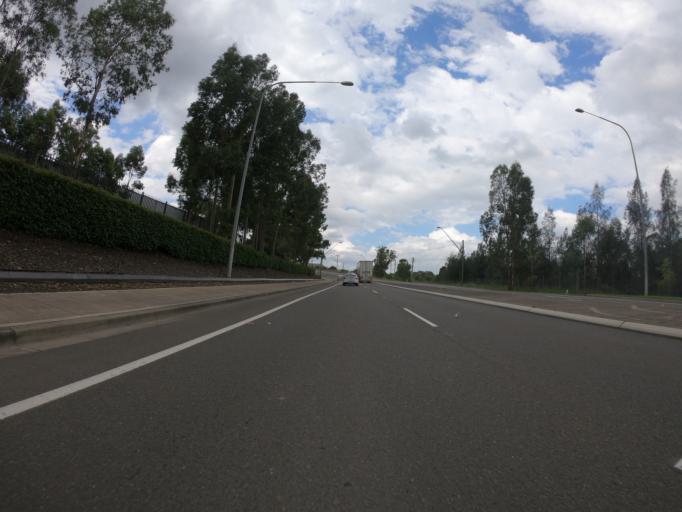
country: AU
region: New South Wales
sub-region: Blacktown
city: Mount Druitt
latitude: -33.8141
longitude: 150.7833
